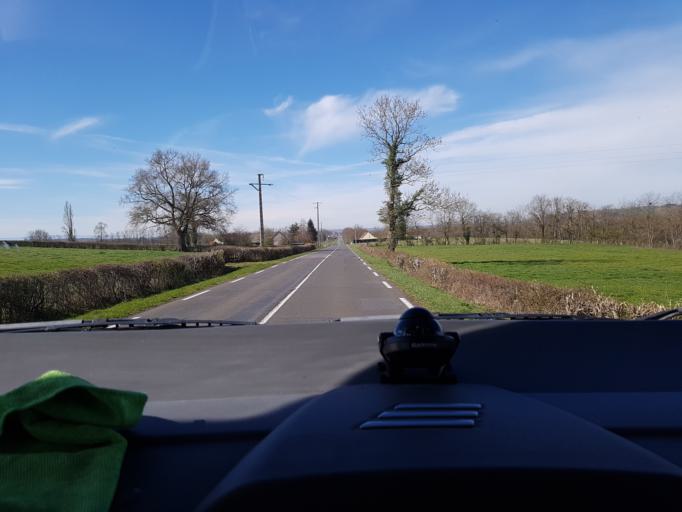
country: FR
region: Bourgogne
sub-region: Departement de Saone-et-Loire
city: Digoin
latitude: 46.5108
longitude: 4.0305
